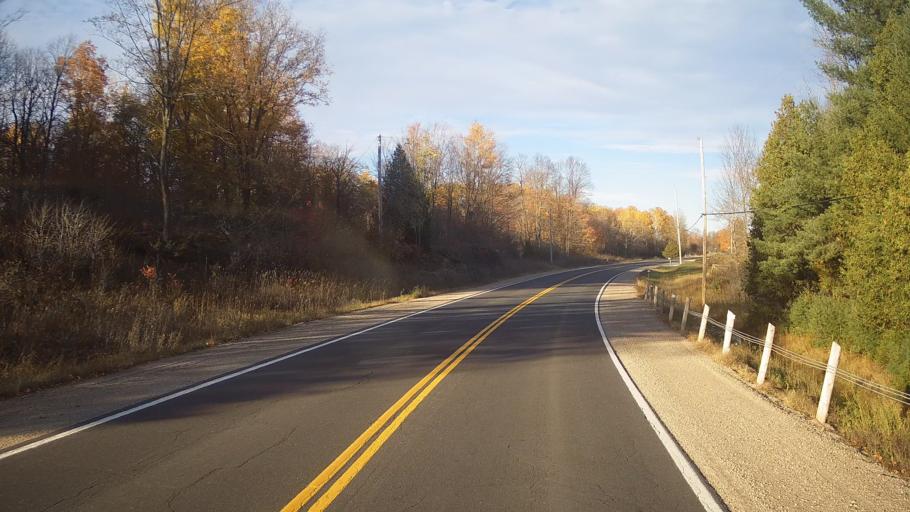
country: CA
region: Ontario
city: Perth
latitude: 44.7983
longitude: -76.3391
